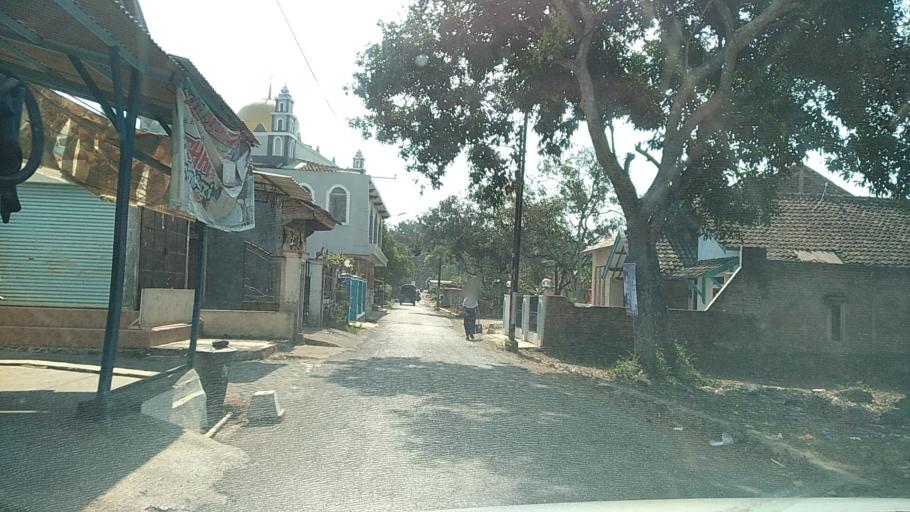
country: ID
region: Central Java
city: Ungaran
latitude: -7.0690
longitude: 110.3147
